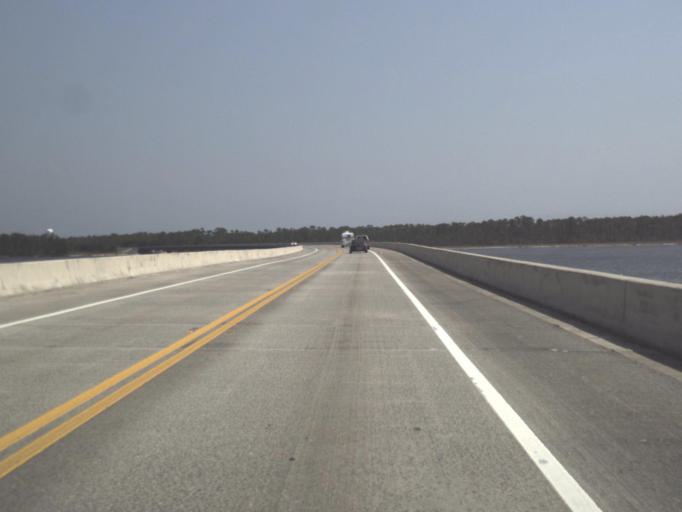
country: US
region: Florida
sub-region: Santa Rosa County
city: Oriole Beach
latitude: 30.4055
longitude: -87.0822
